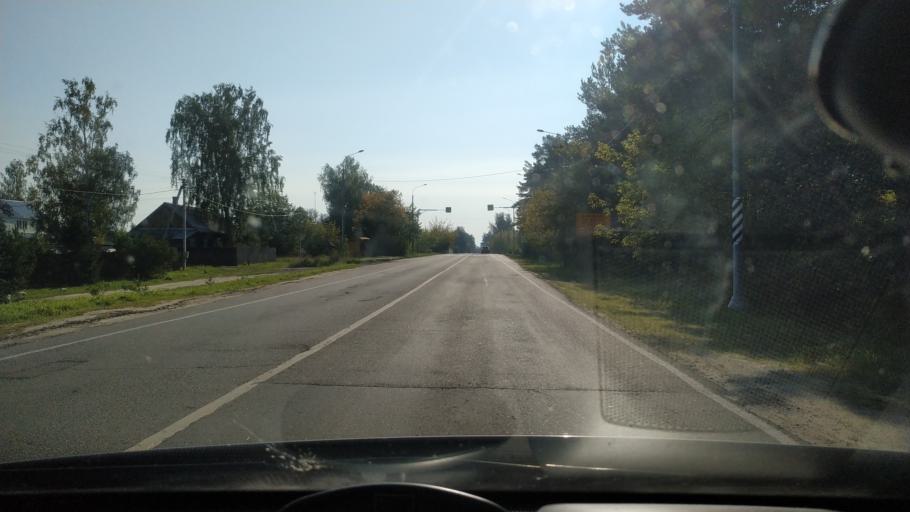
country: RU
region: Moskovskaya
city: Kerva
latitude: 55.5628
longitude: 39.6637
